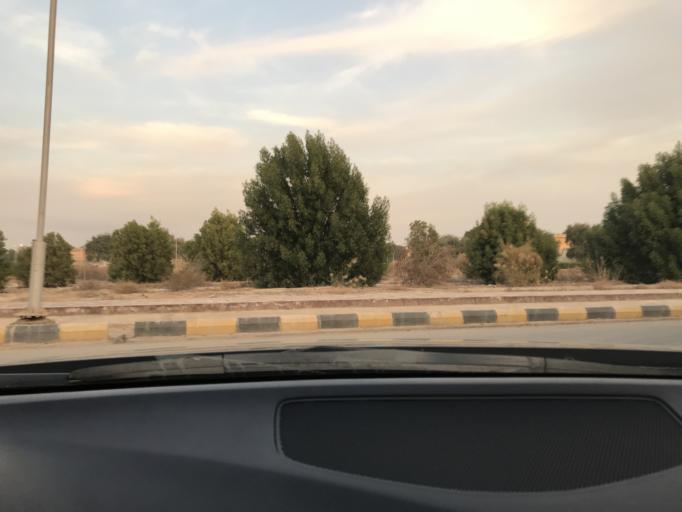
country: IR
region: Khuzestan
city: Ahvaz
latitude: 31.3328
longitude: 48.7337
